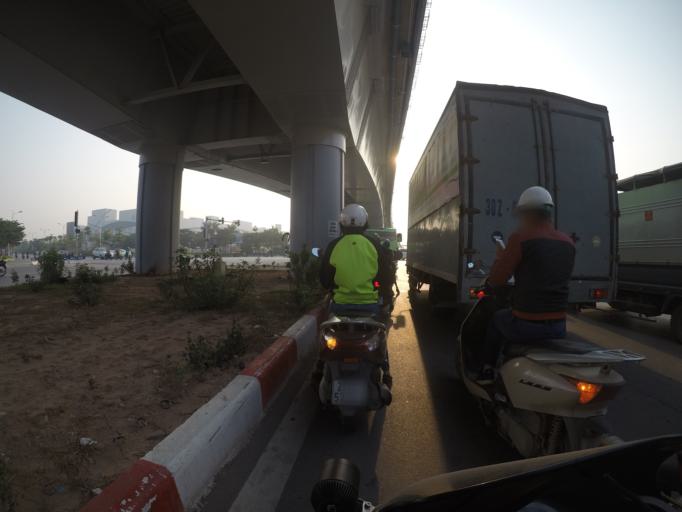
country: VN
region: Ha Noi
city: Trau Quy
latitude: 21.0272
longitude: 105.8961
